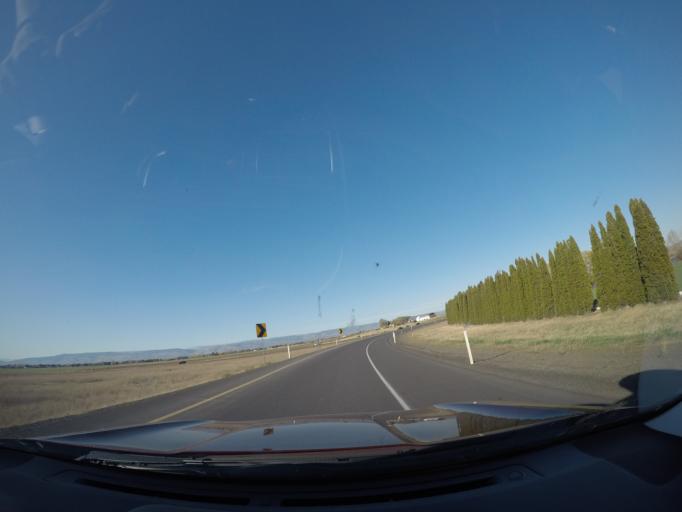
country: US
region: Washington
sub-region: Kittitas County
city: Ellensburg
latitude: 46.9690
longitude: -120.5076
